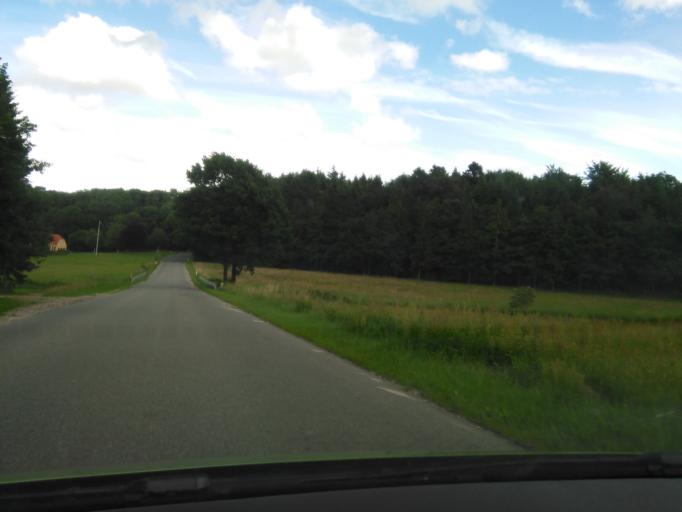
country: DK
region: Central Jutland
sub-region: Horsens Kommune
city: Braedstrup
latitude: 55.9825
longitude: 9.5521
